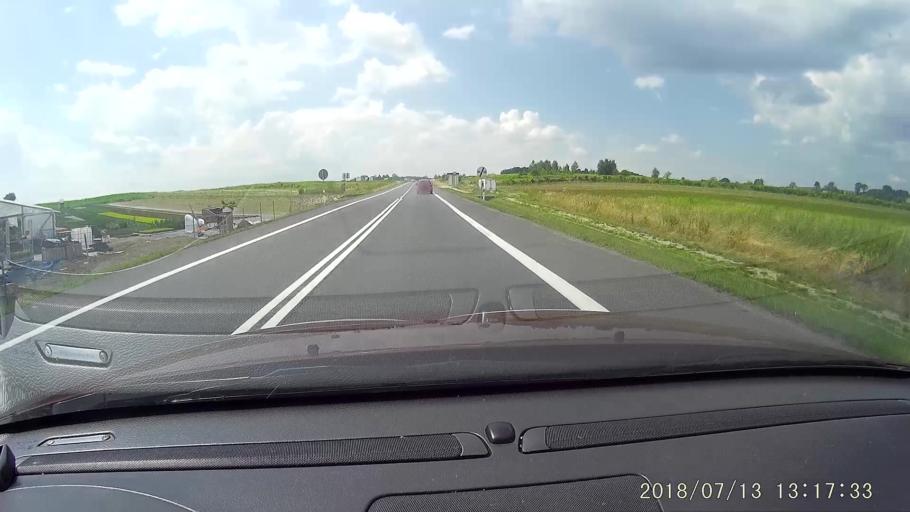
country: PL
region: Lower Silesian Voivodeship
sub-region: Powiat lubanski
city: Pisarzowice
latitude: 51.1345
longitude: 15.2531
